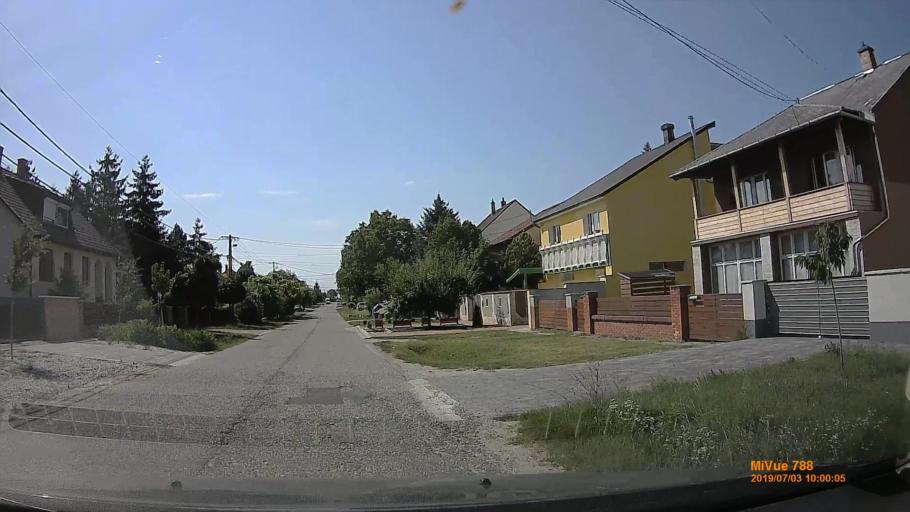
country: HU
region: Gyor-Moson-Sopron
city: Toltestava
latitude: 47.7093
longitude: 17.7241
